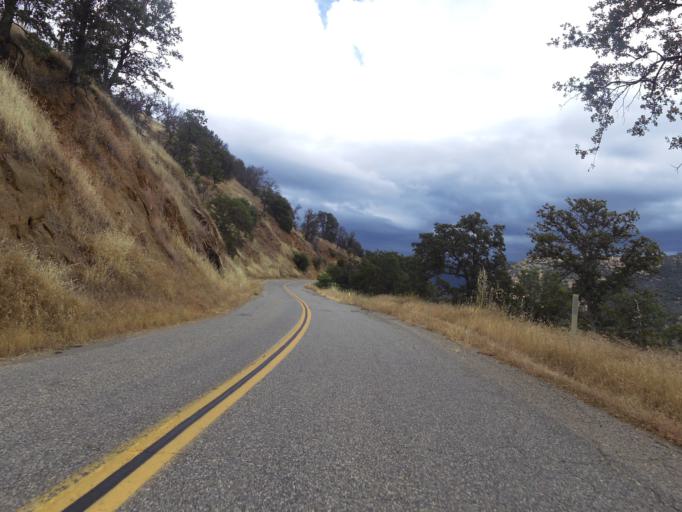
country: US
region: California
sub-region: Madera County
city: Ahwahnee
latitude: 37.3355
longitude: -119.7691
